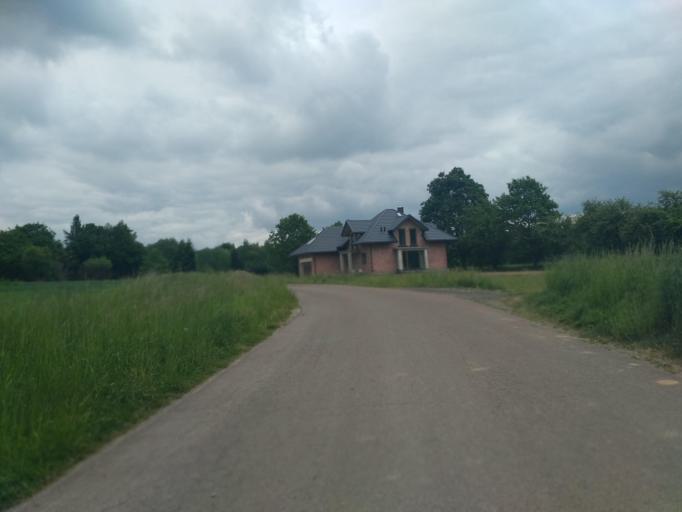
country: PL
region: Subcarpathian Voivodeship
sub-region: Powiat krosnienski
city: Jedlicze
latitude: 49.6861
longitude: 21.6528
